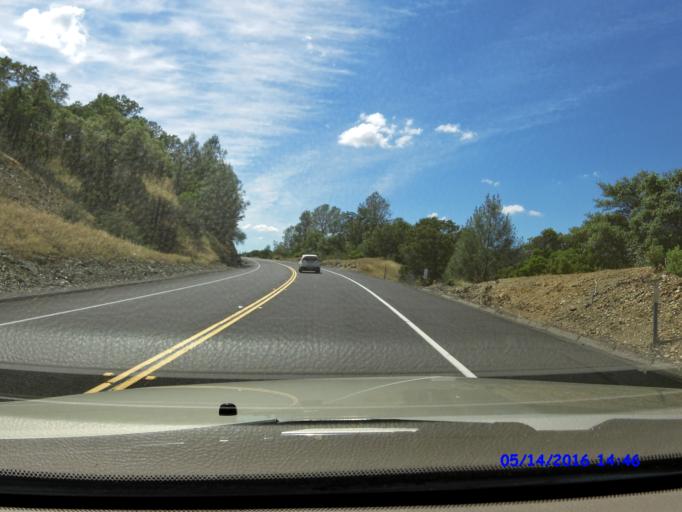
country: US
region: California
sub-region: Tuolumne County
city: Jamestown
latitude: 37.8505
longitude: -120.3941
